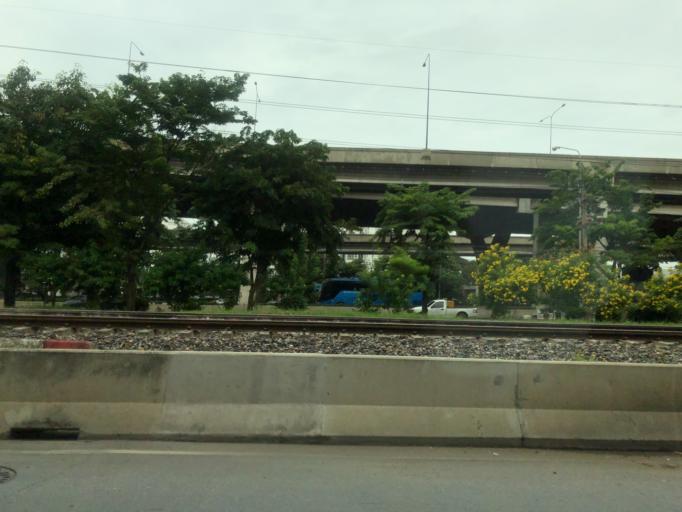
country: TH
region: Bangkok
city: Lak Si
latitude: 13.8915
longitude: 100.5849
